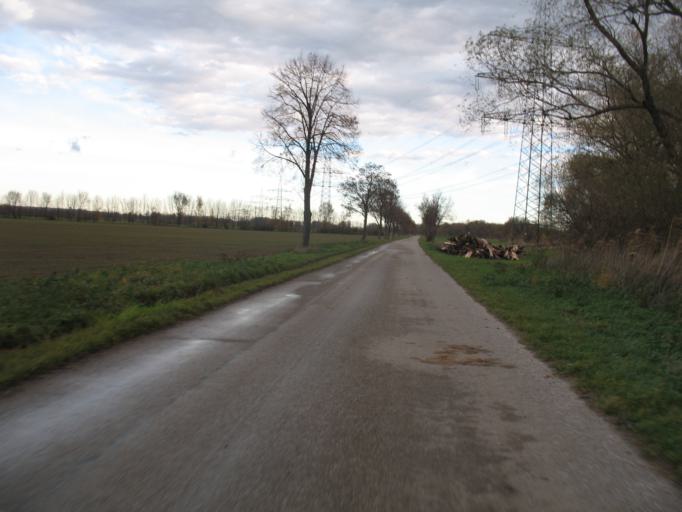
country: AT
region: Lower Austria
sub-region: Politischer Bezirk Modling
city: Munchendorf
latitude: 48.0467
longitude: 16.3963
